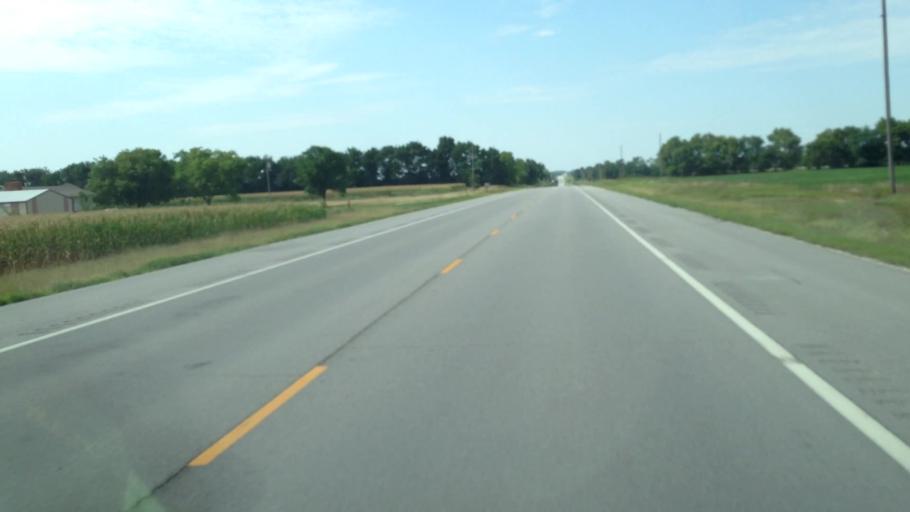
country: US
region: Kansas
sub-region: Labette County
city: Altamont
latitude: 37.2567
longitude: -95.2671
